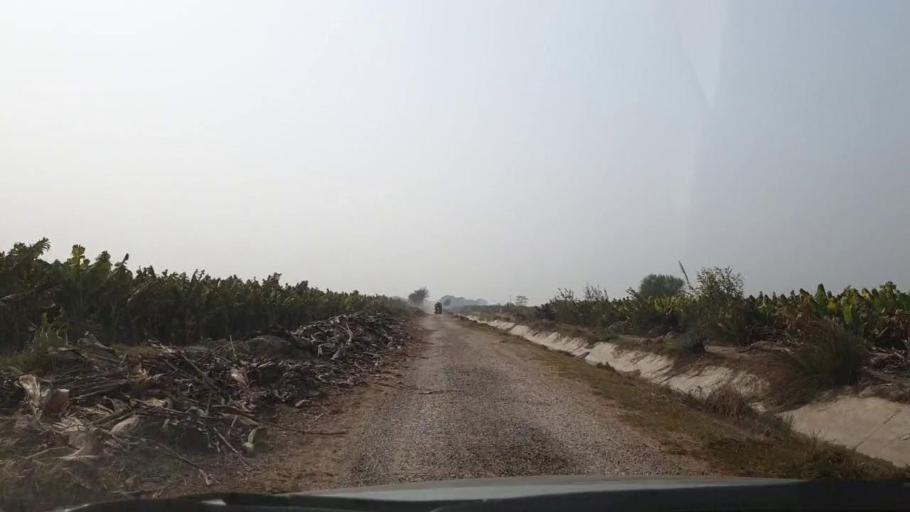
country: PK
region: Sindh
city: Matiari
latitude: 25.6387
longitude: 68.5124
